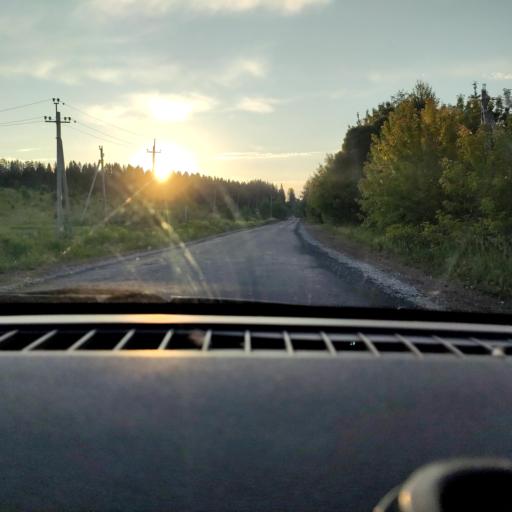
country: RU
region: Perm
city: Sylva
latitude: 57.8459
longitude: 56.7096
